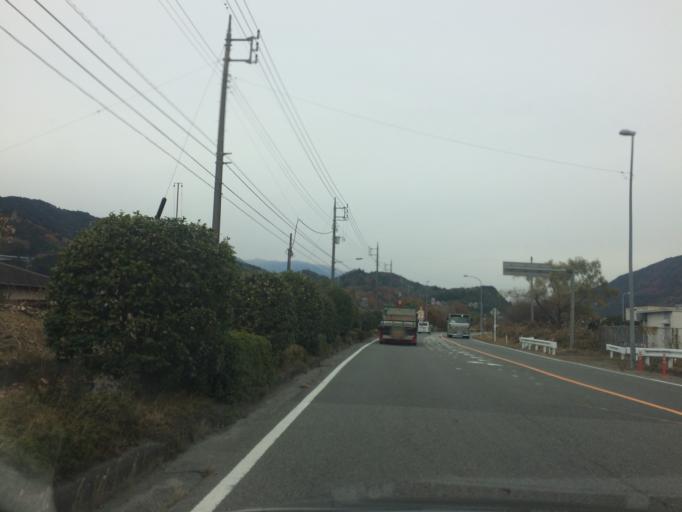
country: JP
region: Shizuoka
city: Fujinomiya
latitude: 35.2434
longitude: 138.4836
